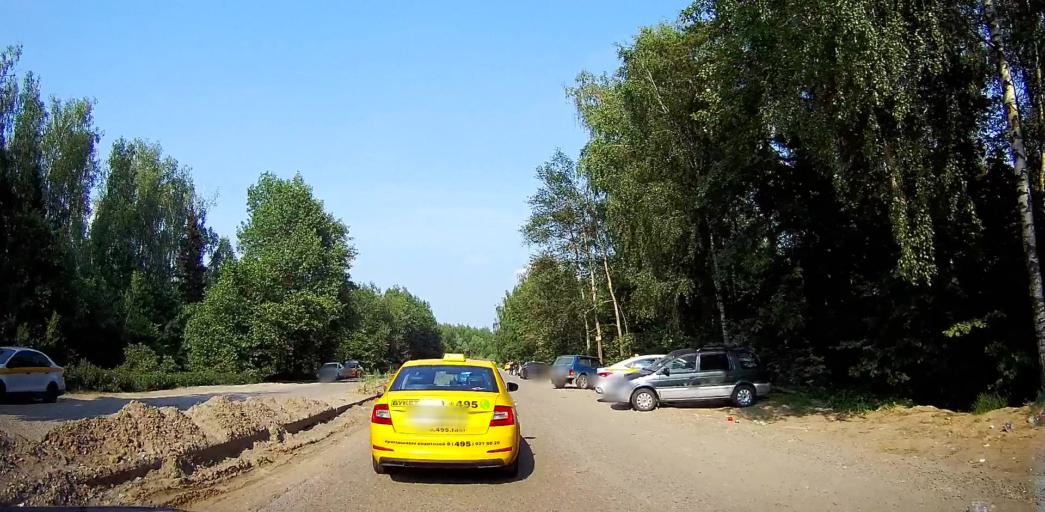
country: RU
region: Moskovskaya
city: Yakovlevskoye
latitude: 55.4307
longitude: 37.8877
